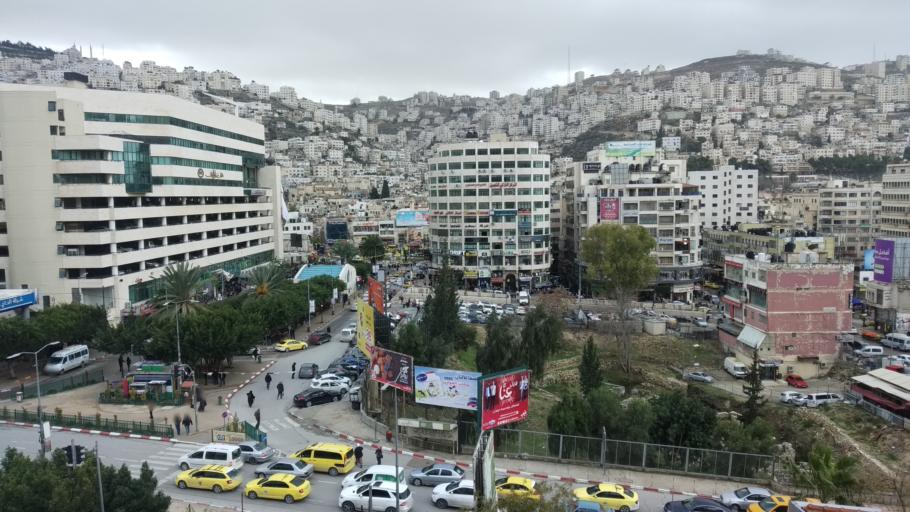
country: PS
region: West Bank
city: Nablus
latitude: 32.2234
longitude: 35.2622
